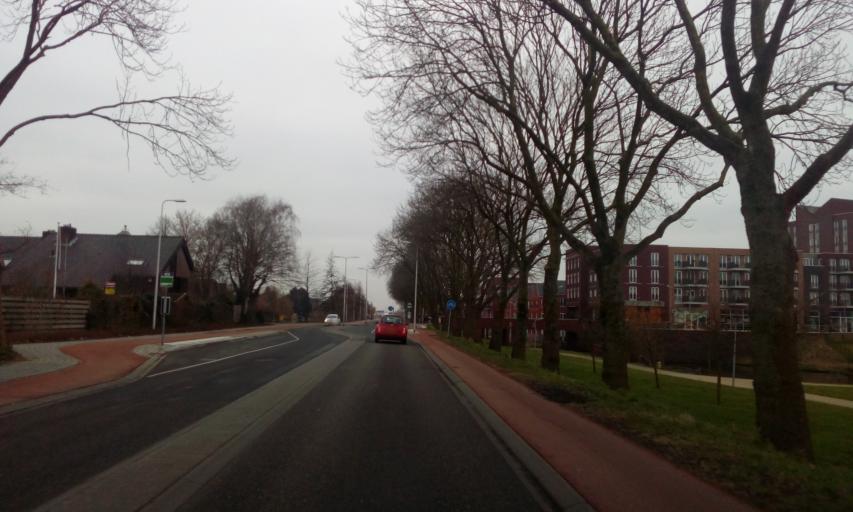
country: NL
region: South Holland
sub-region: Gemeente Waddinxveen
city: Waddinxveen
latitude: 52.0430
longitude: 4.6536
